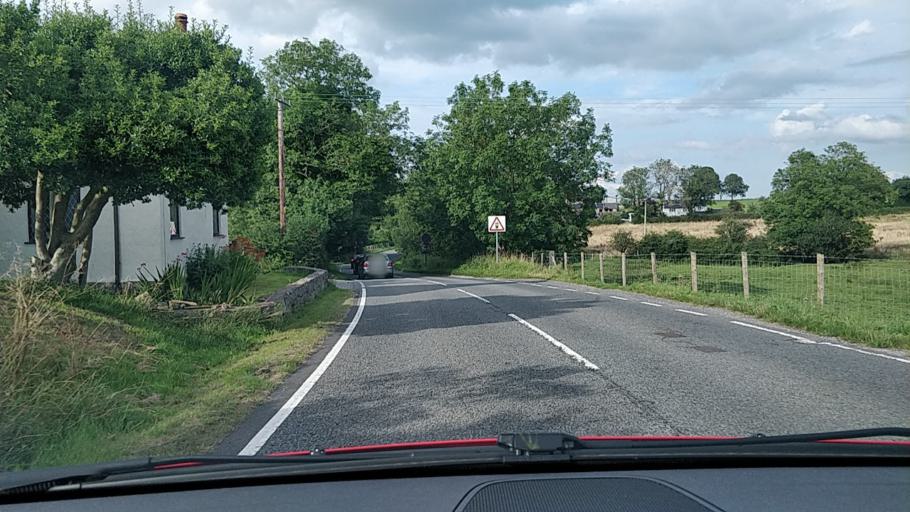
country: GB
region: Wales
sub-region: Denbighshire
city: Llandegla
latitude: 53.0850
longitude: -3.1461
